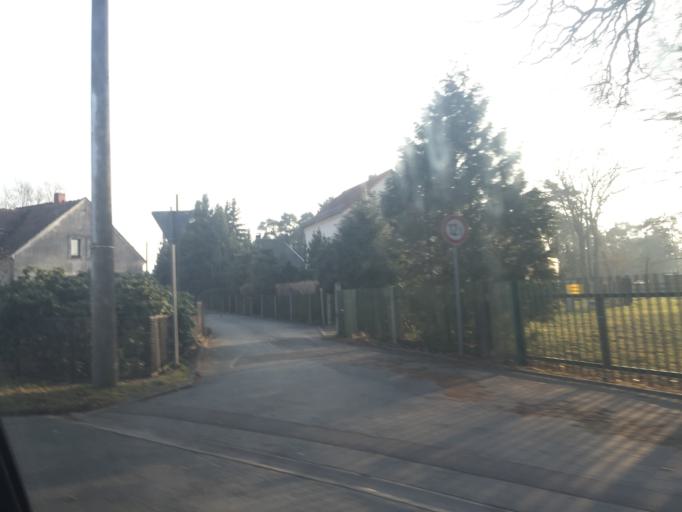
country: DE
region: Saxony
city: Heidenau
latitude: 51.0012
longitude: 13.8982
